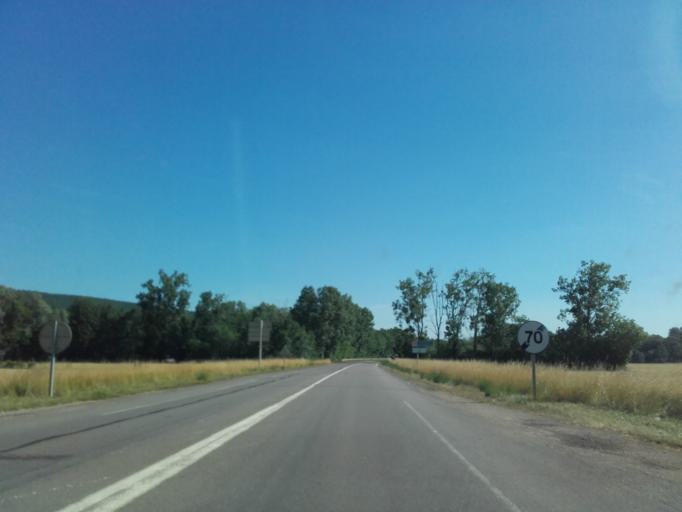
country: FR
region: Bourgogne
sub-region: Departement de Saone-et-Loire
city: Chagny
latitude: 46.9087
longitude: 4.7120
